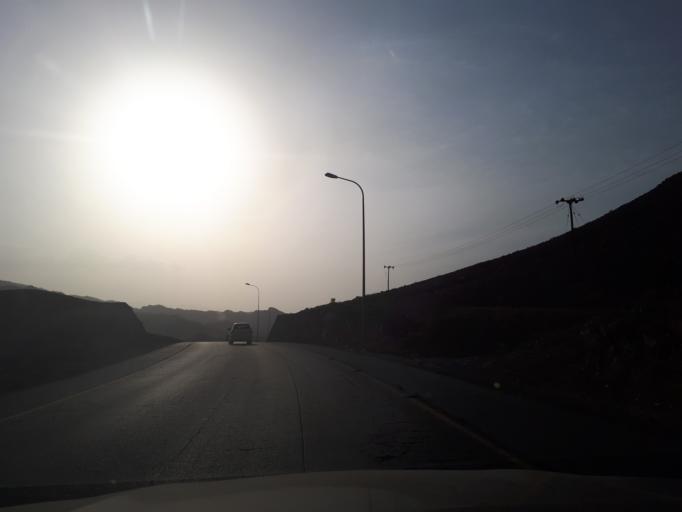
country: OM
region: Muhafazat ad Dakhiliyah
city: Sufalat Sama'il
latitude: 23.1860
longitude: 58.0956
